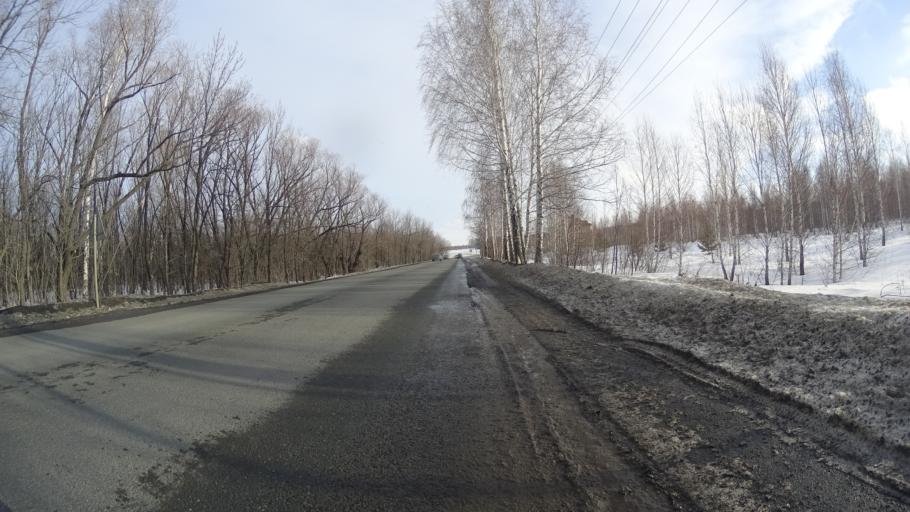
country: RU
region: Chelyabinsk
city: Sargazy
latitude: 55.1359
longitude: 61.2838
